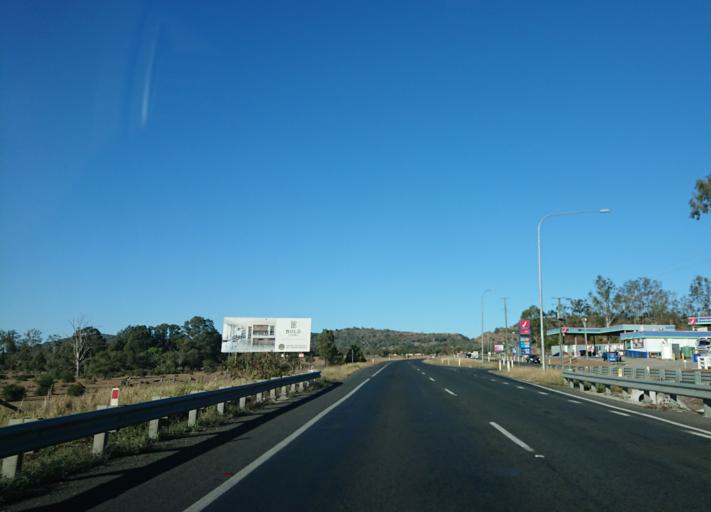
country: AU
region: Queensland
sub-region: Ipswich
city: Thagoona
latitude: -27.5506
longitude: 152.4975
